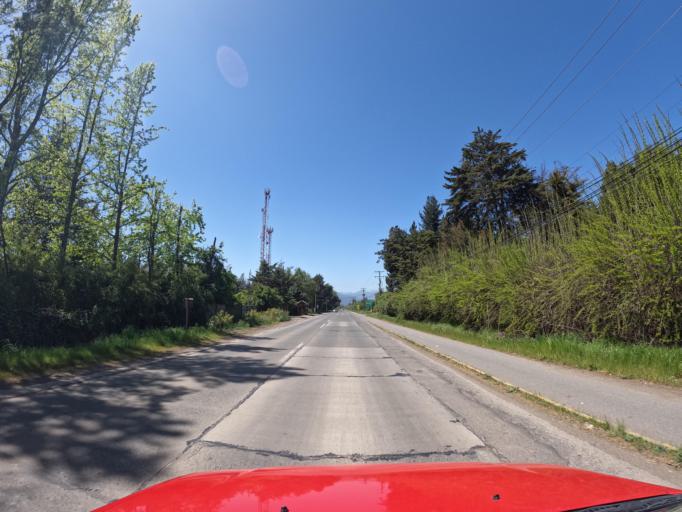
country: CL
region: Maule
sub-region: Provincia de Linares
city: Linares
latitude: -35.8312
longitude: -71.5198
